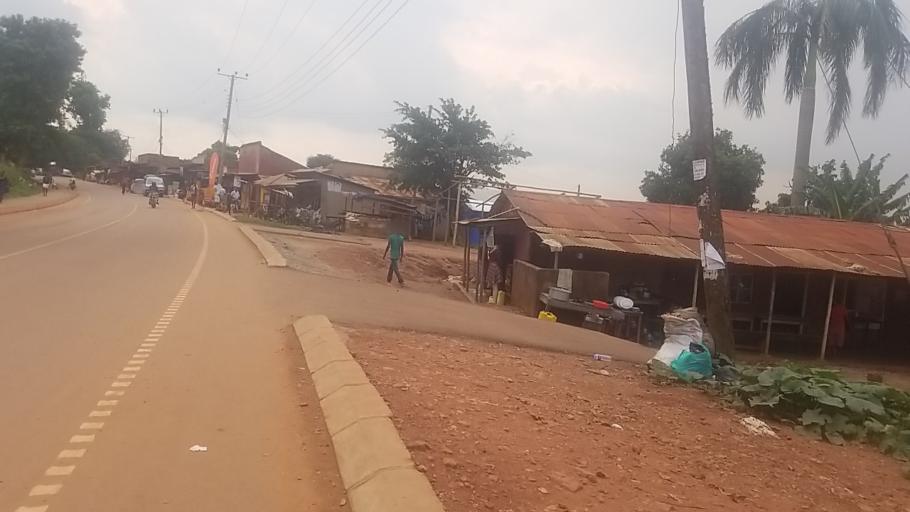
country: UG
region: Central Region
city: Kampala Central Division
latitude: 0.3399
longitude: 32.5693
